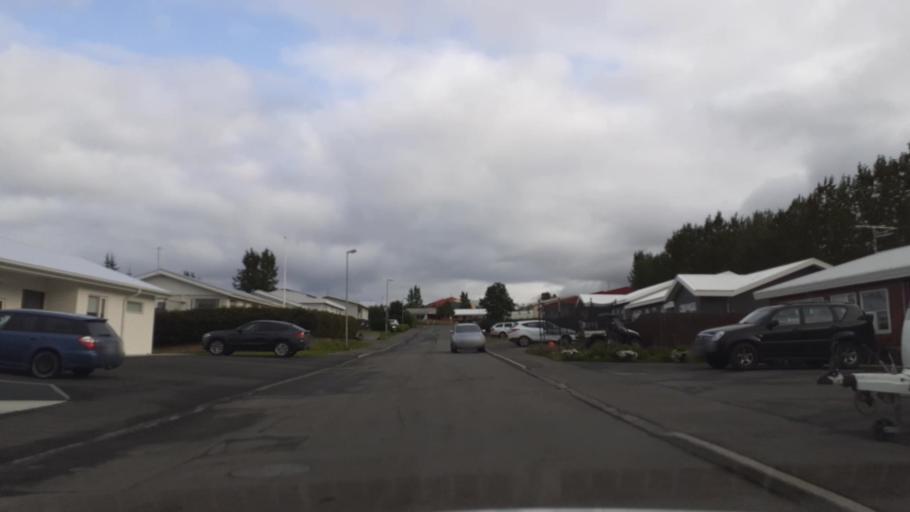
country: IS
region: Northeast
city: Akureyri
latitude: 65.7461
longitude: -18.0823
